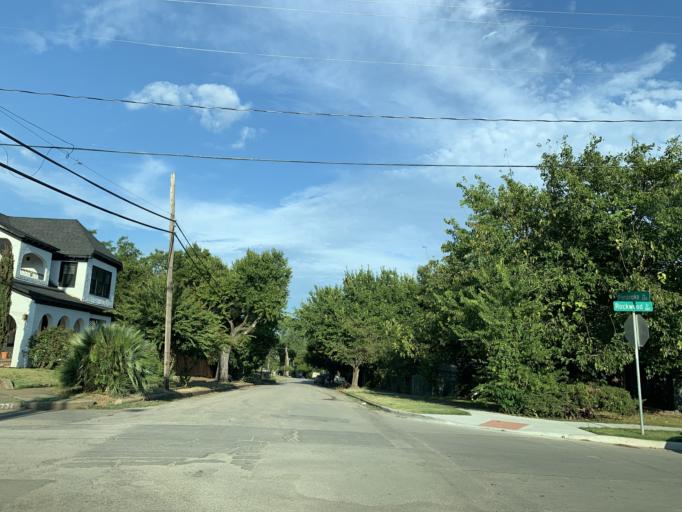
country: US
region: Texas
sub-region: Dallas County
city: Dallas
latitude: 32.7381
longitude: -96.8217
